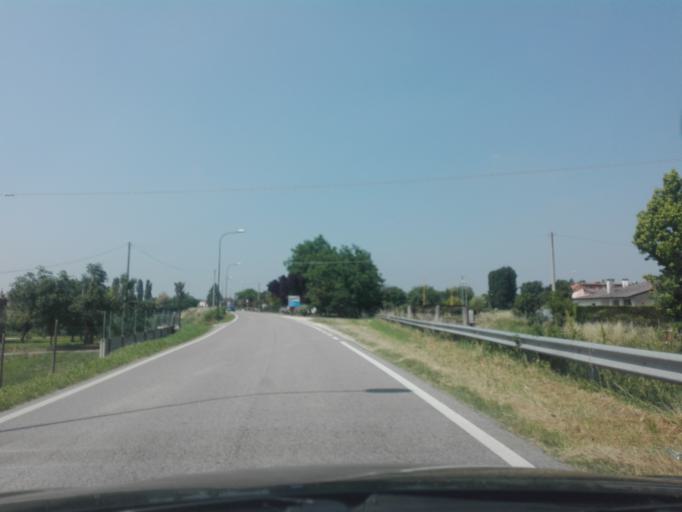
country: IT
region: Veneto
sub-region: Provincia di Rovigo
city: Villadose
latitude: 45.0689
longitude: 11.8784
